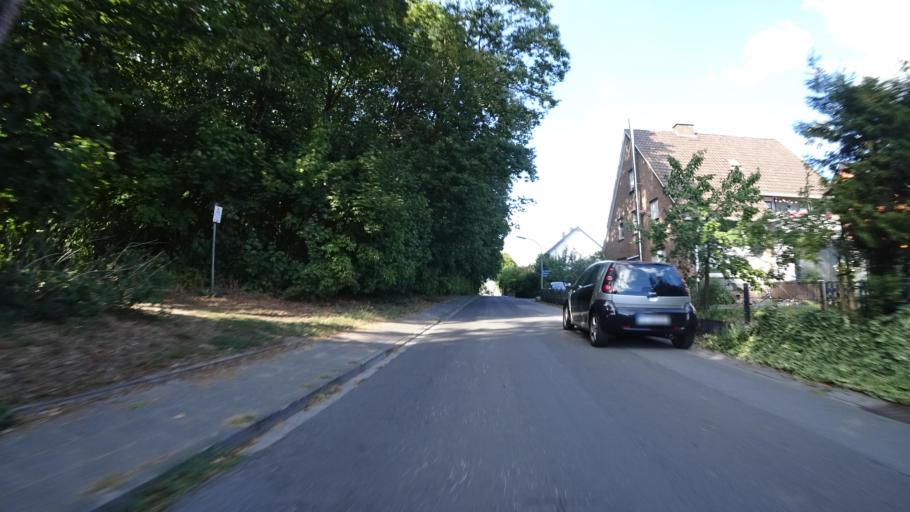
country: DE
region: North Rhine-Westphalia
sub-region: Regierungsbezirk Detmold
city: Rheda-Wiedenbruck
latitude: 51.8536
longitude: 8.3053
